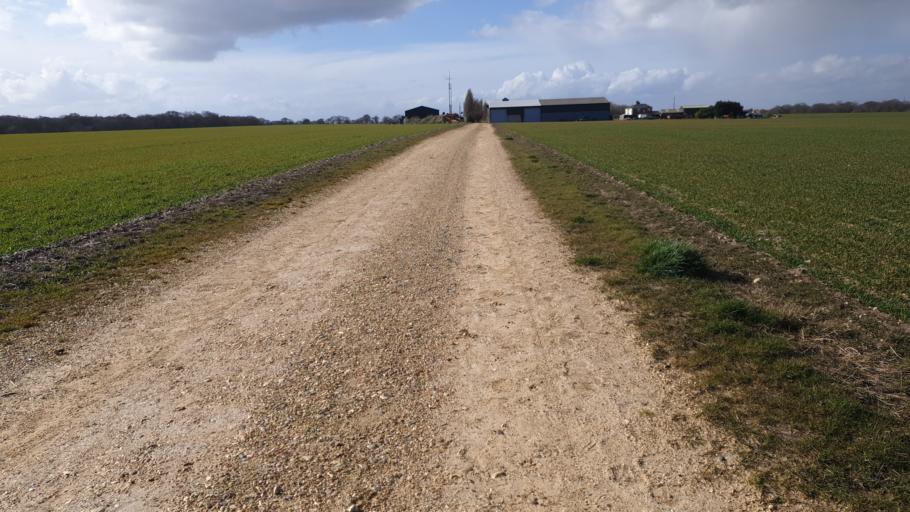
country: GB
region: England
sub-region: Essex
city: Little Clacton
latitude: 51.8488
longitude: 1.1469
